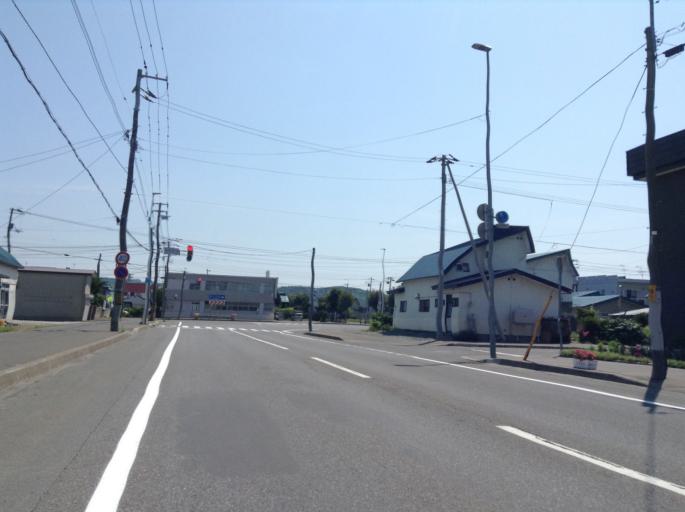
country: JP
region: Hokkaido
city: Nayoro
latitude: 44.3615
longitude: 142.4559
